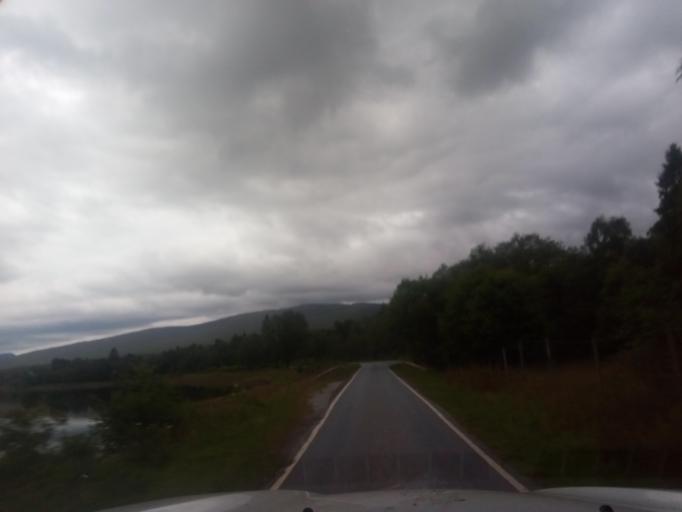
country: GB
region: Scotland
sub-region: Highland
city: Fort William
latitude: 56.8507
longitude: -5.3240
